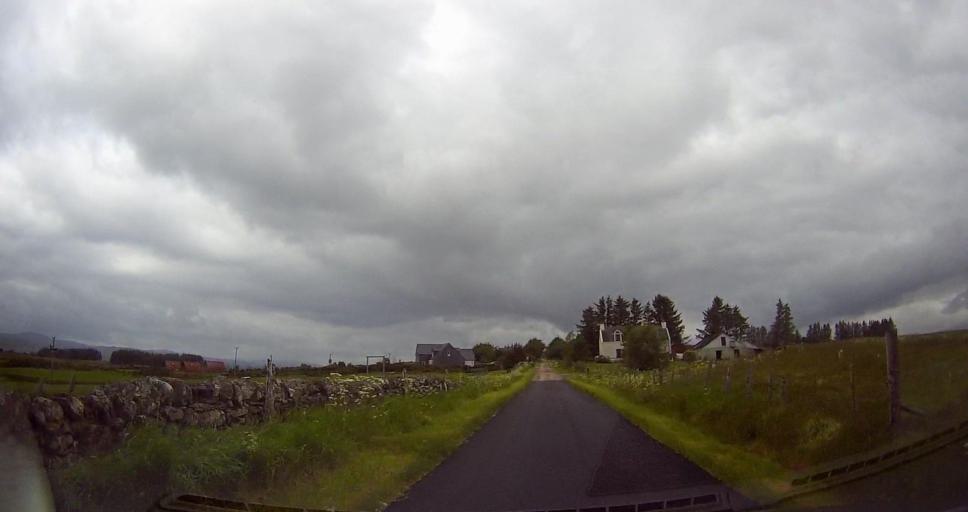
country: GB
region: Scotland
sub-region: Highland
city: Alness
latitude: 58.0734
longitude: -4.4375
